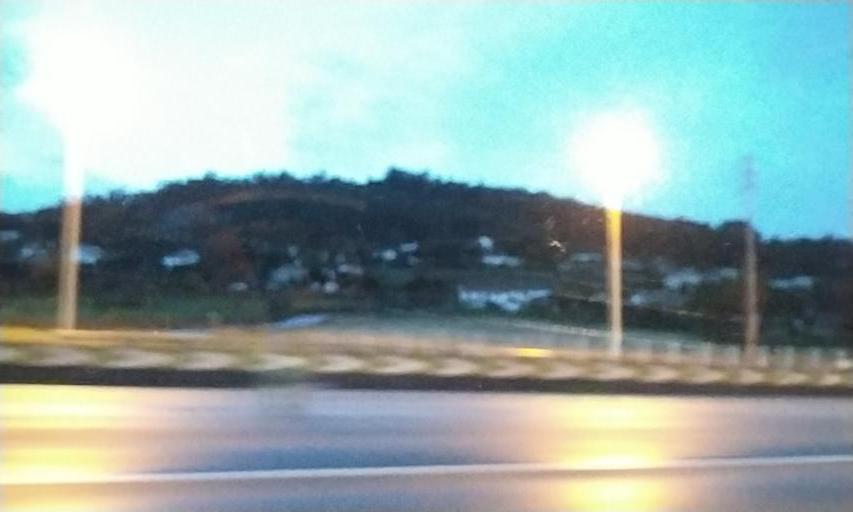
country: PT
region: Braga
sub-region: Braga
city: Oliveira
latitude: 41.5035
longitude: -8.4413
